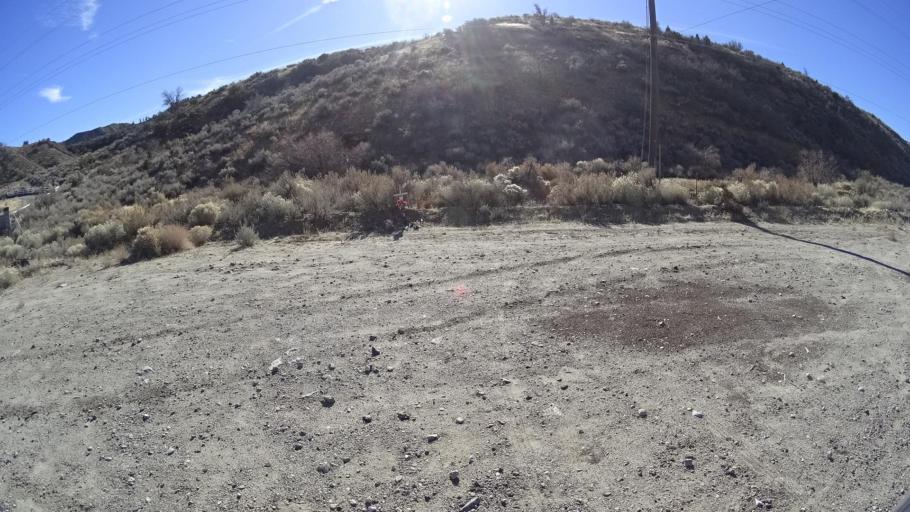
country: US
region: California
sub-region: Kern County
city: Frazier Park
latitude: 34.8188
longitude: -118.9146
